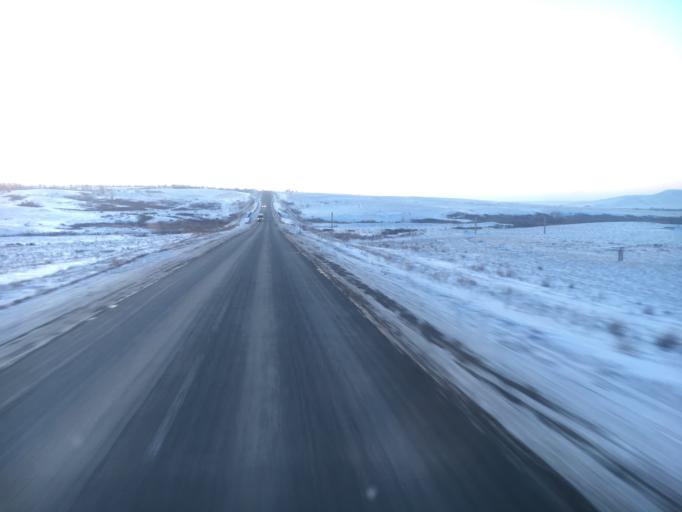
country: KZ
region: Aqtoebe
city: Aqtobe
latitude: 50.2834
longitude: 57.7656
